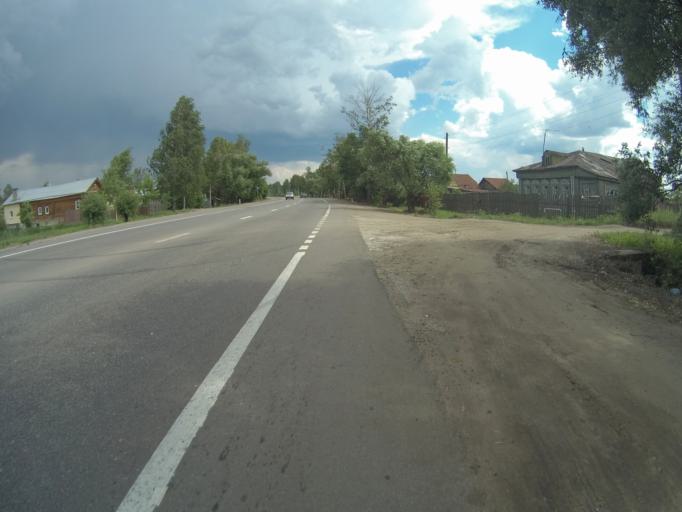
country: RU
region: Vladimir
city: Orgtrud
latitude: 56.2084
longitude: 40.6723
